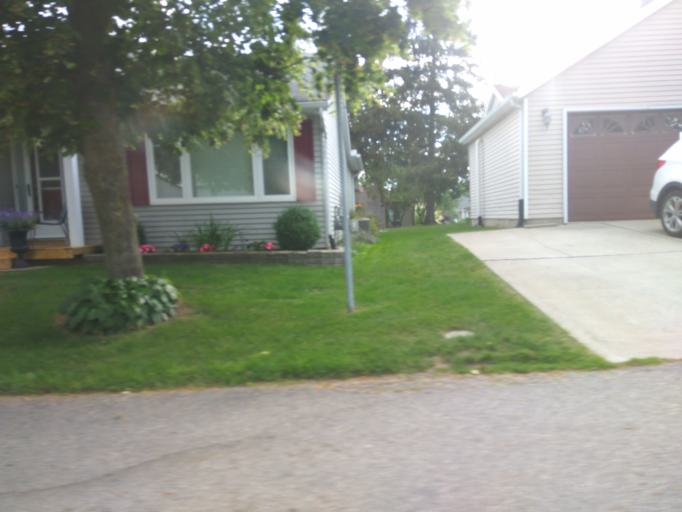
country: CA
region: Ontario
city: Kitchener
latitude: 43.3740
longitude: -80.6920
